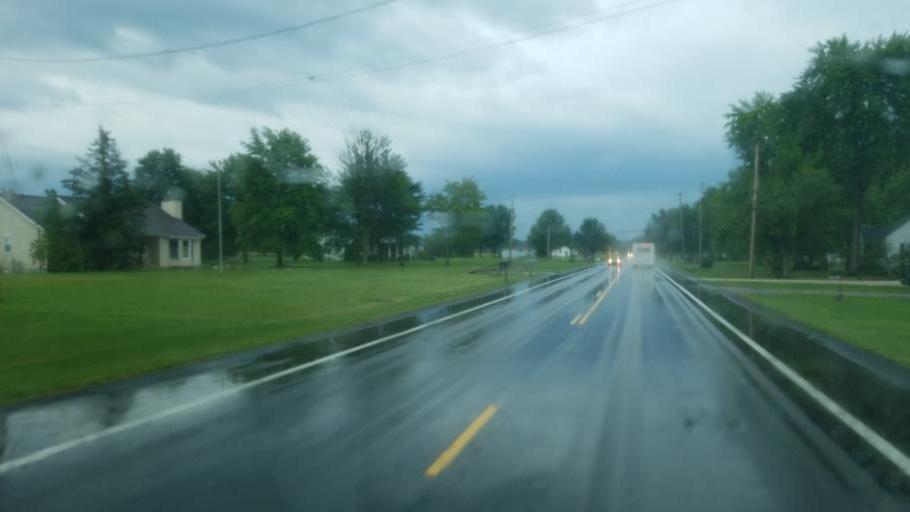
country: US
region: Ohio
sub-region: Trumbull County
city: Champion Heights
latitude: 41.3280
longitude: -80.8575
